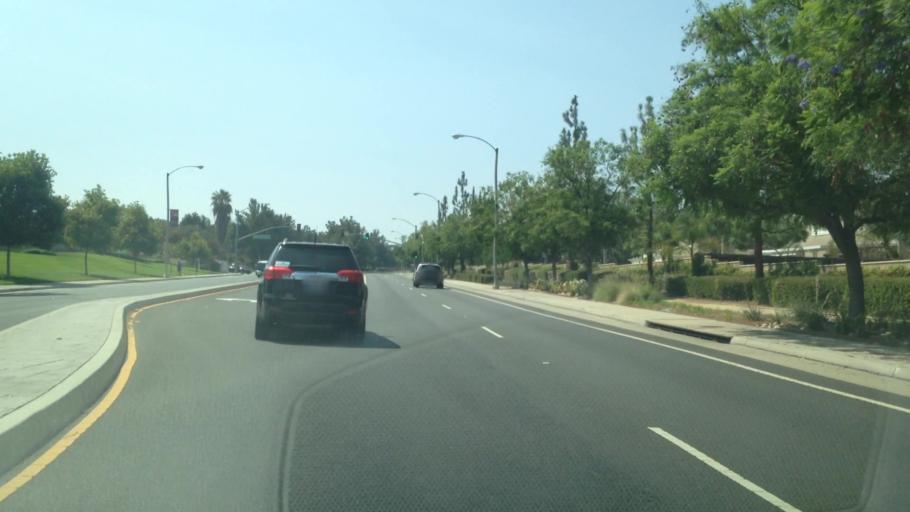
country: US
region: California
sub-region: Riverside County
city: Woodcrest
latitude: 33.9015
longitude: -117.3261
